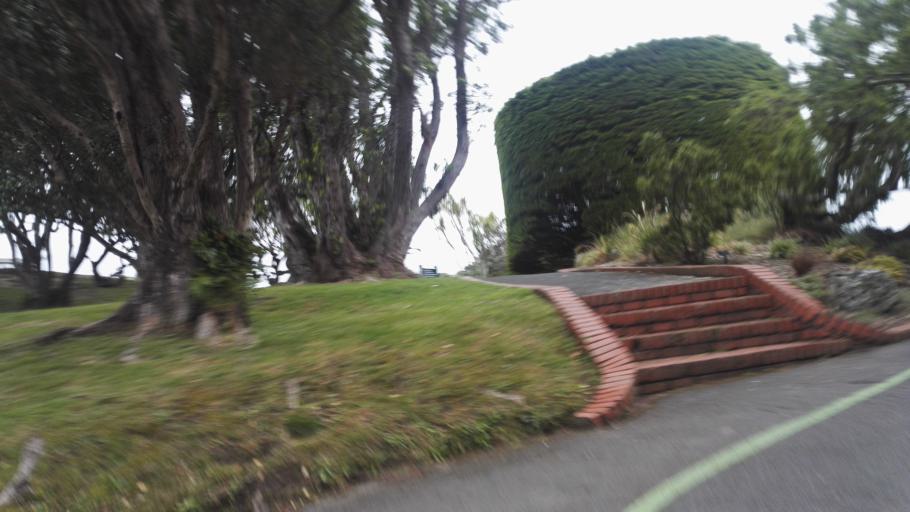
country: NZ
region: Wellington
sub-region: Wellington City
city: Kelburn
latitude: -41.2852
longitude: 174.7673
